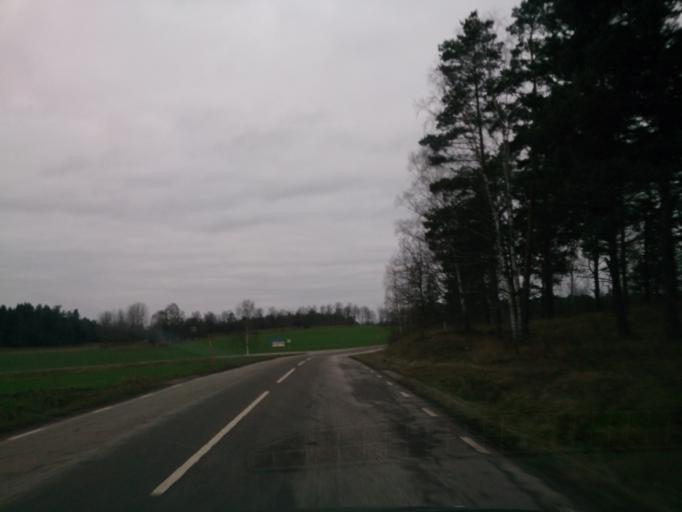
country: SE
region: OEstergoetland
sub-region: Norrkopings Kommun
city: Kimstad
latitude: 58.3971
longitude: 15.9547
